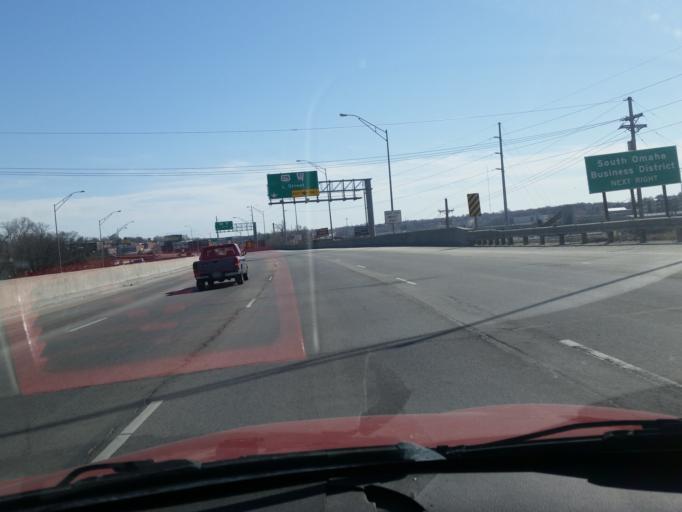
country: US
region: Nebraska
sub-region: Douglas County
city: Omaha
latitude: 41.2165
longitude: -95.9535
